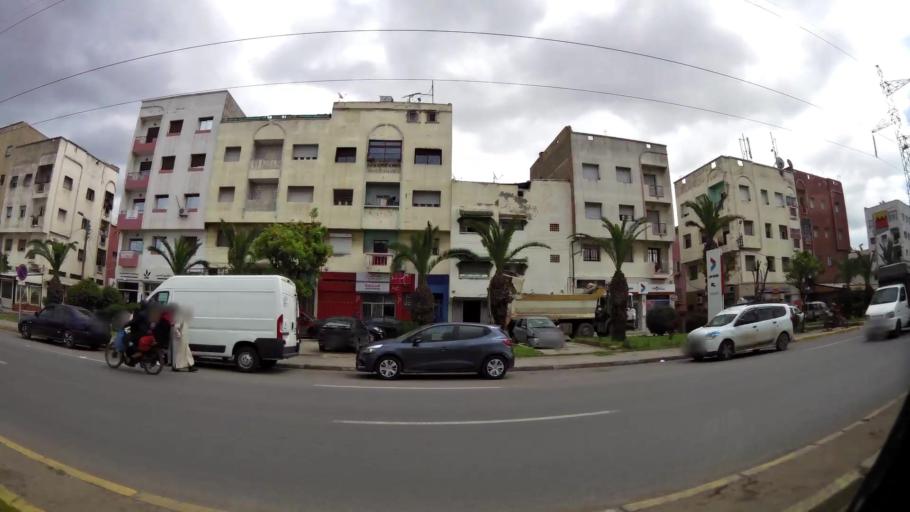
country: MA
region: Grand Casablanca
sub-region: Mediouna
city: Tit Mellil
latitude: 33.5802
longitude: -7.5432
